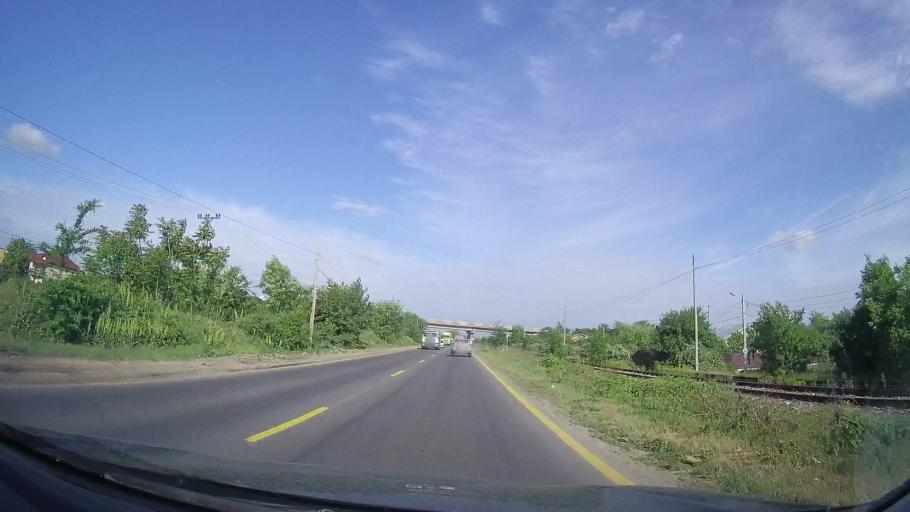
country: RO
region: Ilfov
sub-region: Comuna Magurele
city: Magurele
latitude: 44.3583
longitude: 26.0393
